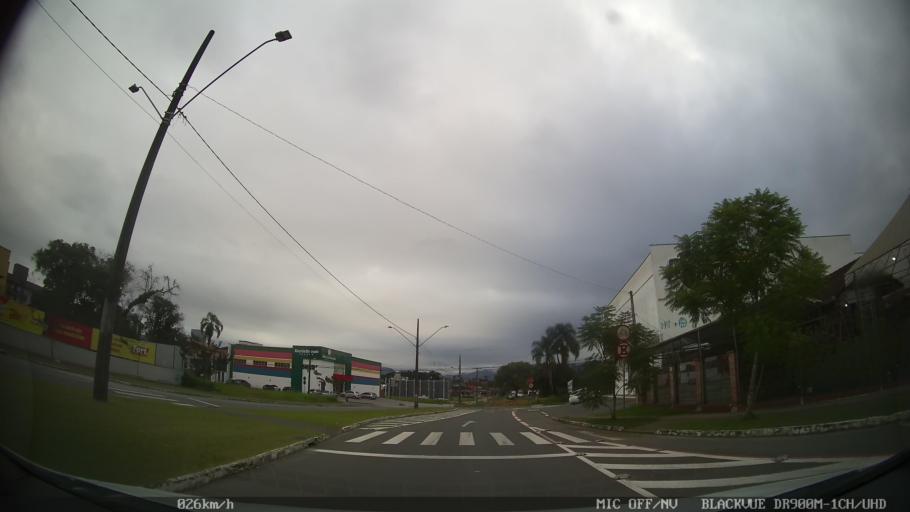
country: BR
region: Santa Catarina
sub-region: Joinville
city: Joinville
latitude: -26.2738
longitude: -48.8777
